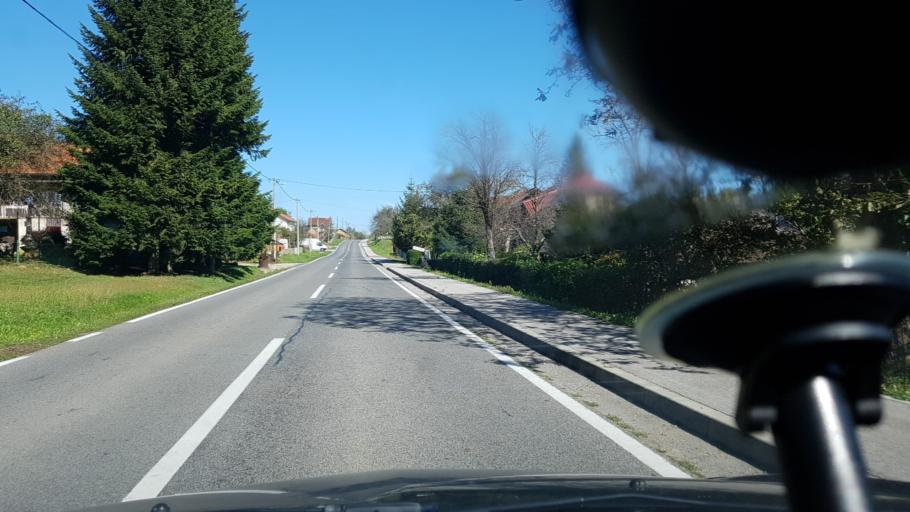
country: HR
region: Zagrebacka
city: Kriz
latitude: 45.7142
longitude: 16.4959
